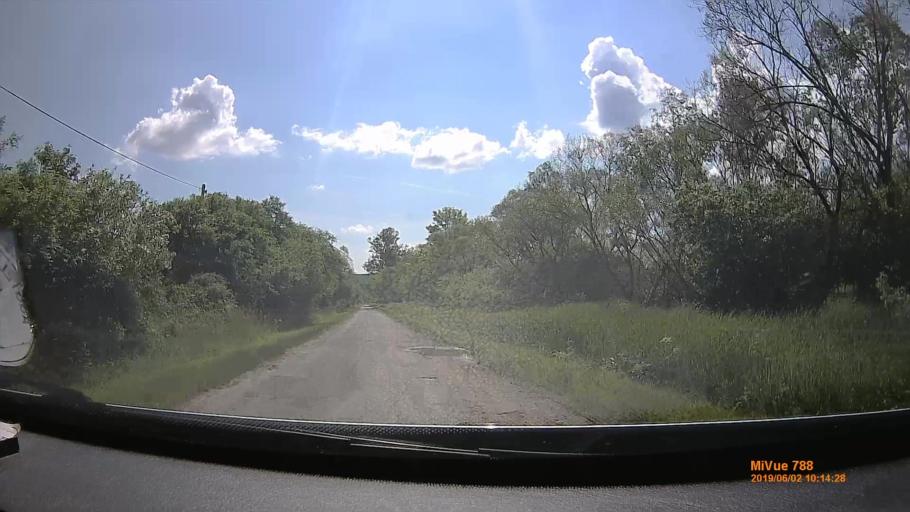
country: HU
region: Borsod-Abauj-Zemplen
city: Szendro
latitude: 48.5097
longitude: 20.7917
